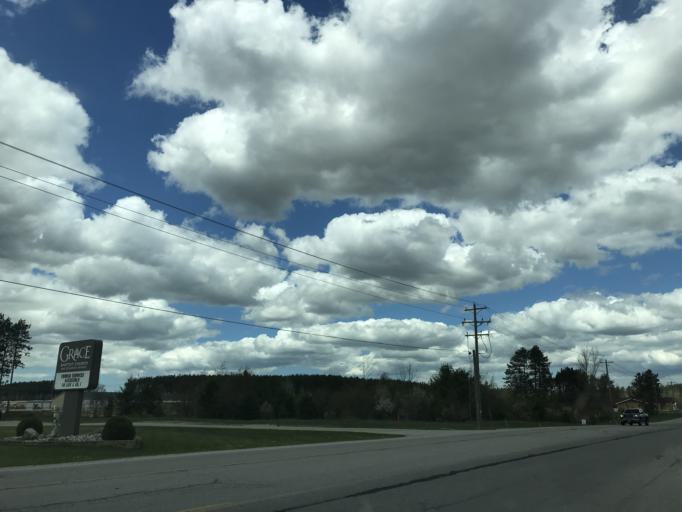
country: US
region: Michigan
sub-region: Otsego County
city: Gaylord
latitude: 45.0252
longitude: -84.7268
